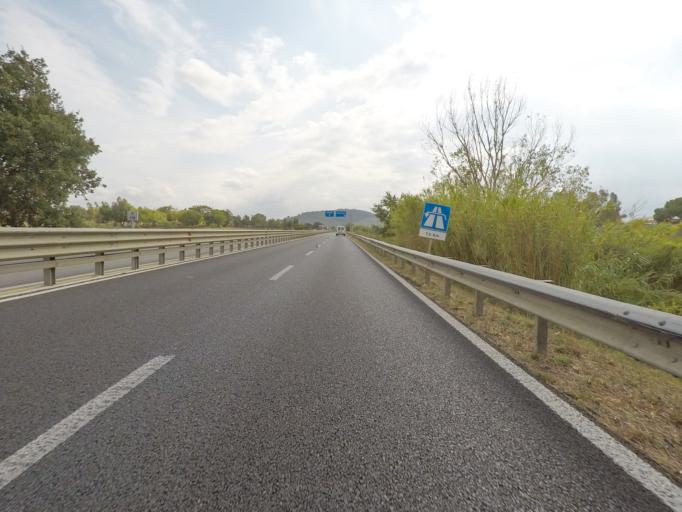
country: IT
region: Tuscany
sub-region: Provincia di Grosseto
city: Grosseto
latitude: 42.7191
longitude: 11.1410
